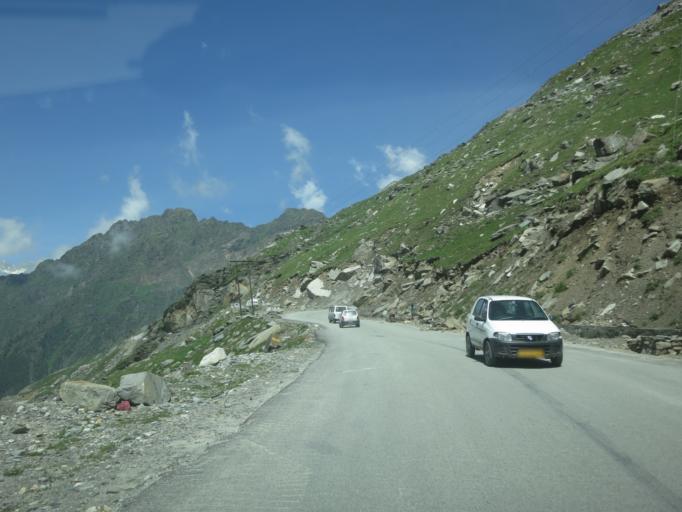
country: IN
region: Himachal Pradesh
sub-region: Kulu
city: Manali
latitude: 32.3565
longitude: 77.2307
